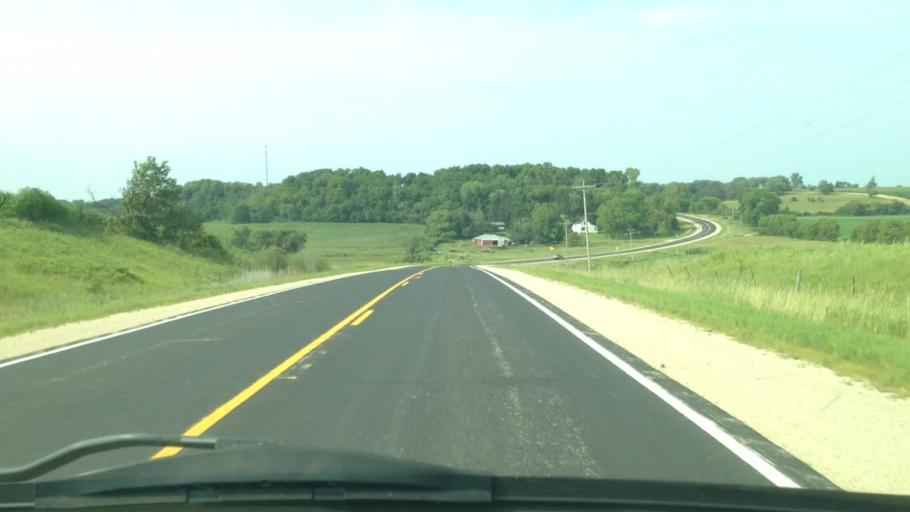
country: US
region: Minnesota
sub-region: Winona County
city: Lewiston
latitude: 43.9207
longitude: -91.9593
